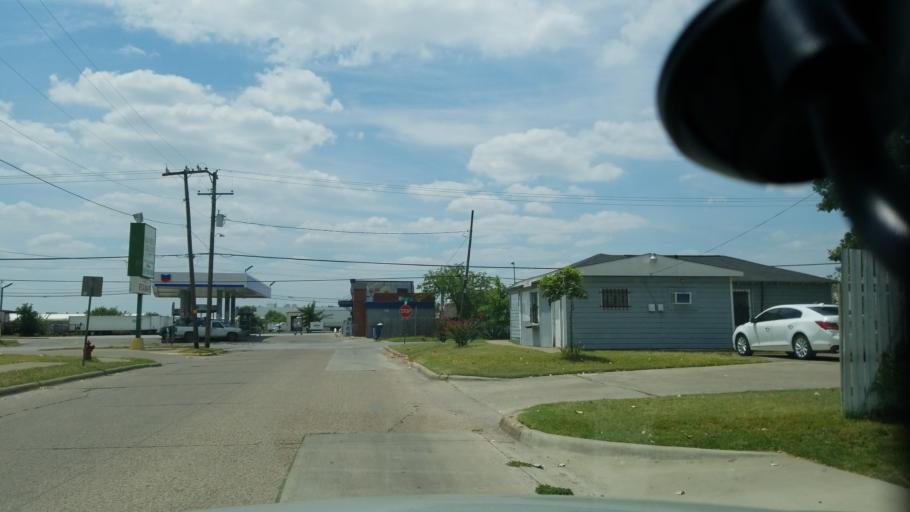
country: US
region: Texas
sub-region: Dallas County
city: Grand Prairie
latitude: 32.7492
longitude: -96.9813
